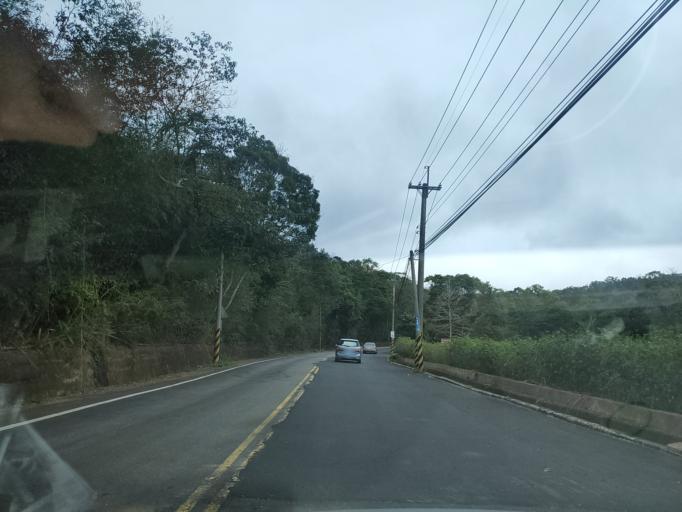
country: TW
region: Taiwan
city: Fengyuan
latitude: 24.3741
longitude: 120.7676
